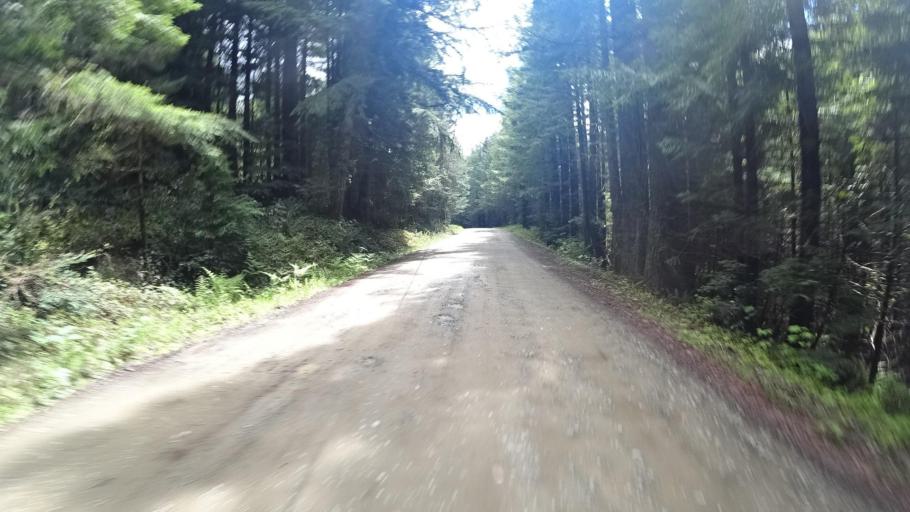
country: US
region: California
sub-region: Humboldt County
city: Blue Lake
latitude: 40.8067
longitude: -123.8838
